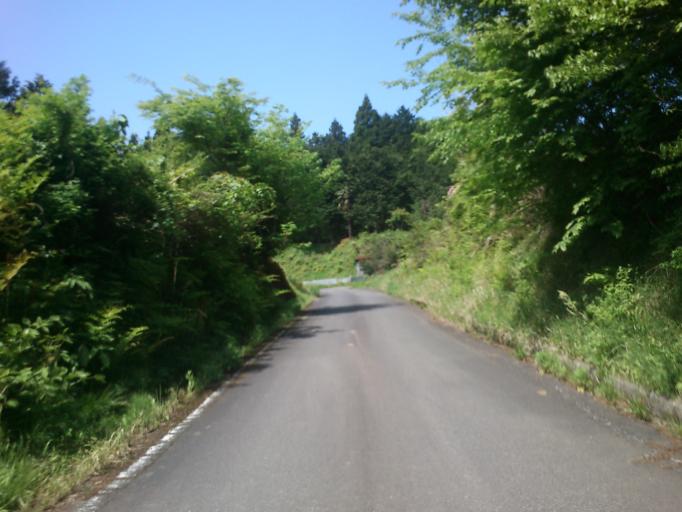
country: JP
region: Kyoto
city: Miyazu
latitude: 35.6673
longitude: 135.2351
